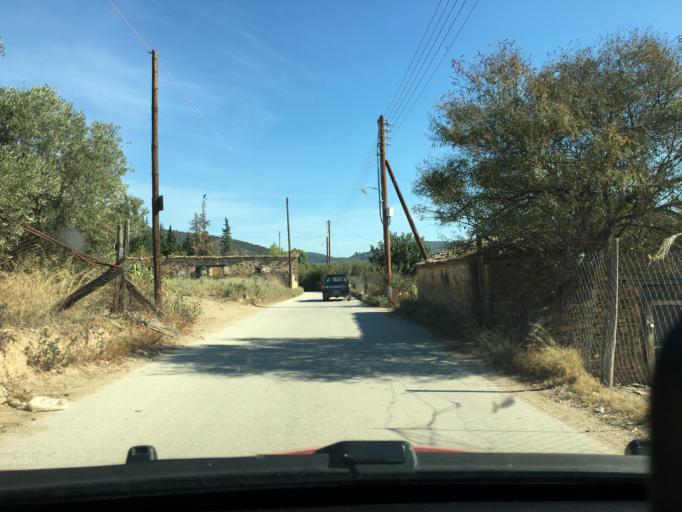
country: GR
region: Central Macedonia
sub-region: Nomos Chalkidikis
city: Ormylia
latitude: 40.2973
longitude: 23.5476
